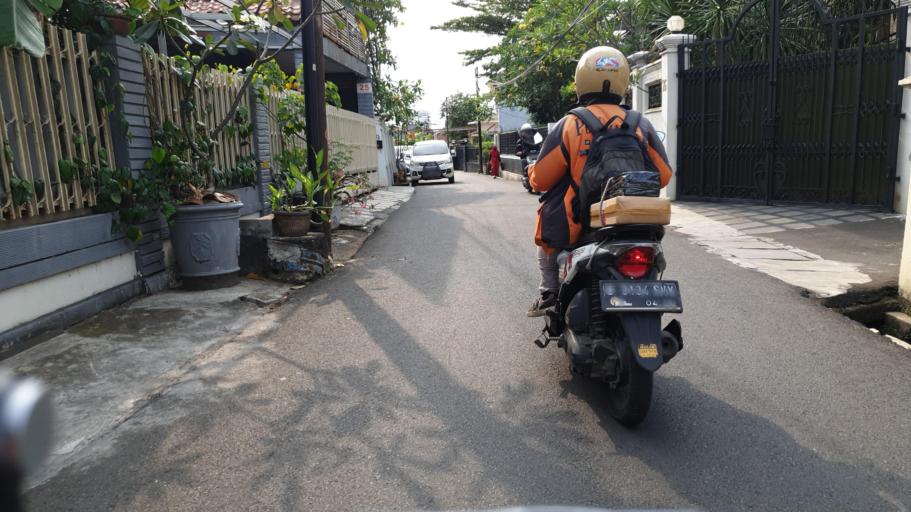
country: ID
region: Jakarta Raya
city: Jakarta
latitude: -6.2757
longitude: 106.7959
